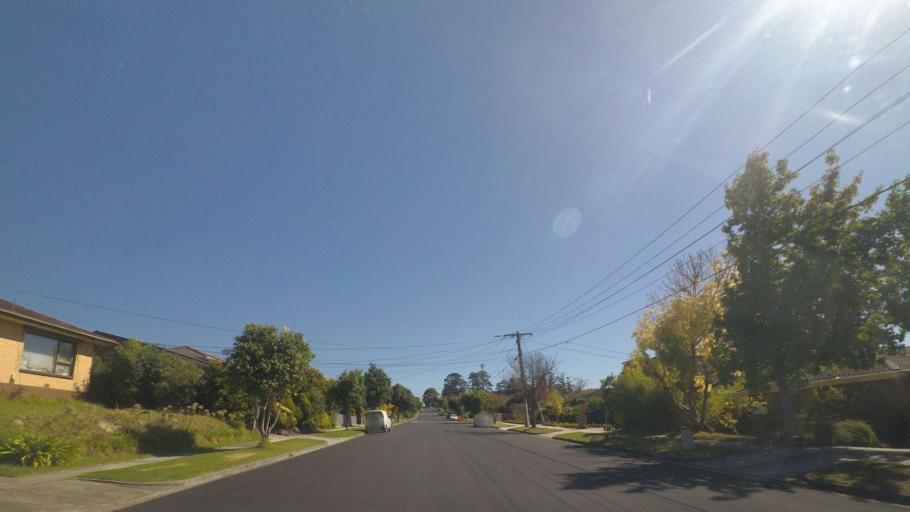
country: AU
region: Victoria
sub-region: Manningham
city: Donvale
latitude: -37.7837
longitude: 145.1698
